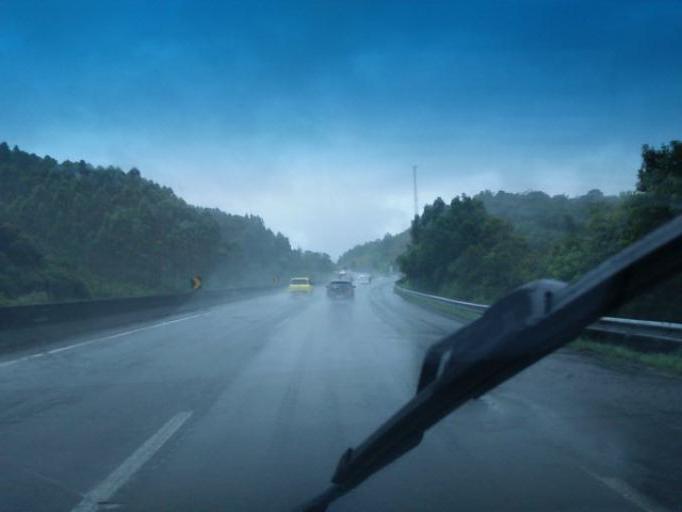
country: BR
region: Parana
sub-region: Campina Grande Do Sul
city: Campina Grande do Sul
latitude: -25.2491
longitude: -48.9081
